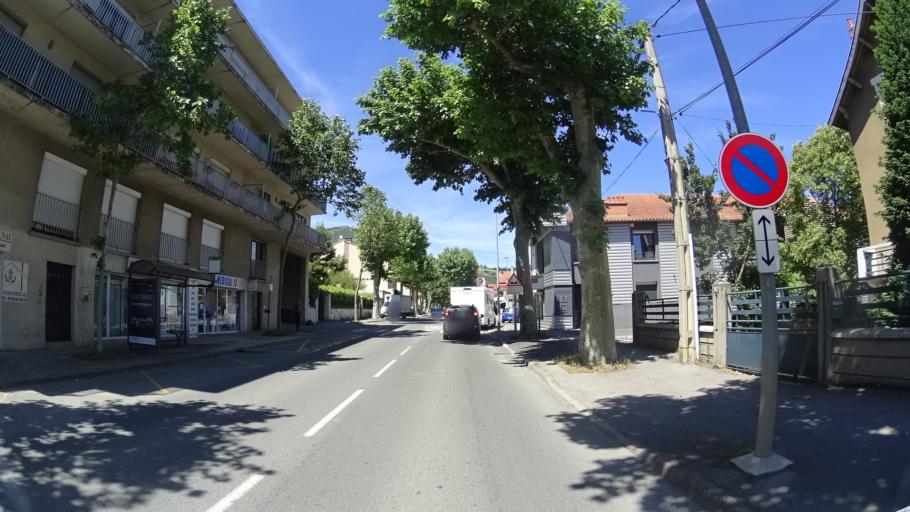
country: FR
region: Midi-Pyrenees
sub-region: Departement de l'Aveyron
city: Millau
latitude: 44.1097
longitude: 3.0817
